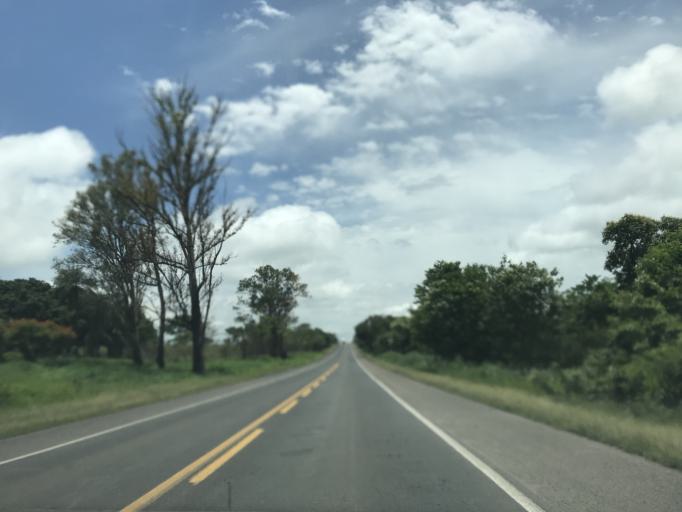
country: BR
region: Minas Gerais
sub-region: Prata
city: Prata
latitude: -19.6280
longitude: -48.9417
